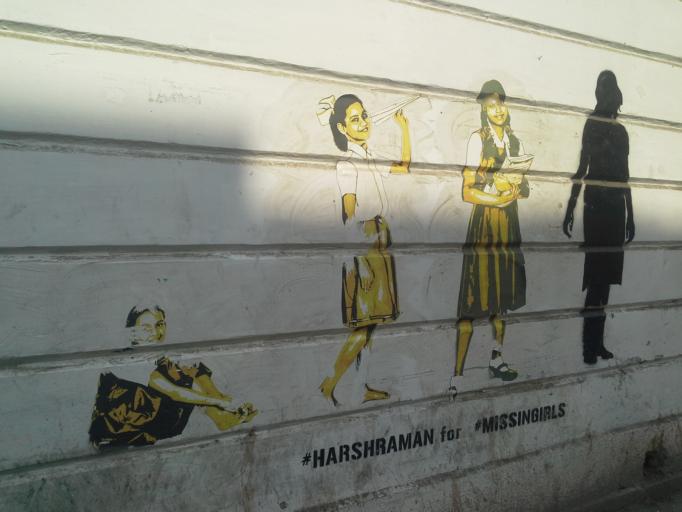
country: IN
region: NCT
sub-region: New Delhi
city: New Delhi
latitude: 28.6306
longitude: 77.2197
